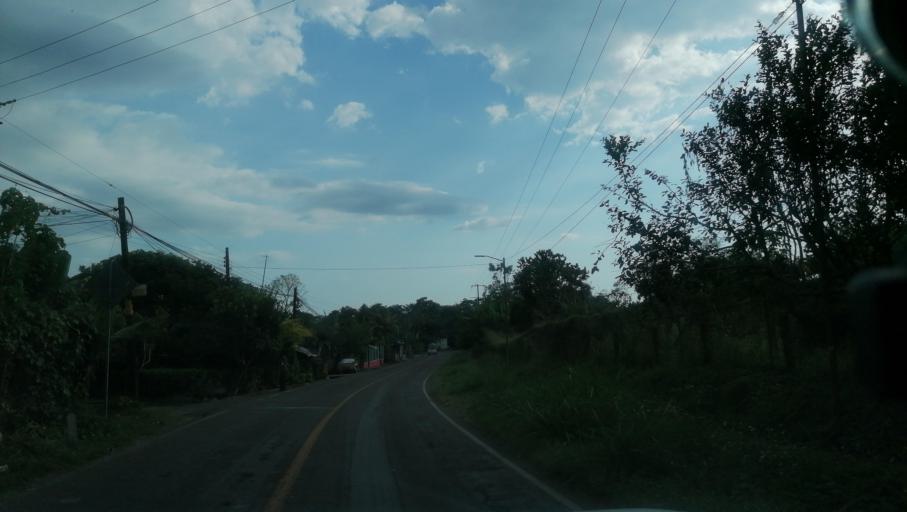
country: MX
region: Chiapas
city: Cacahoatan
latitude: 15.0065
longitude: -92.1561
